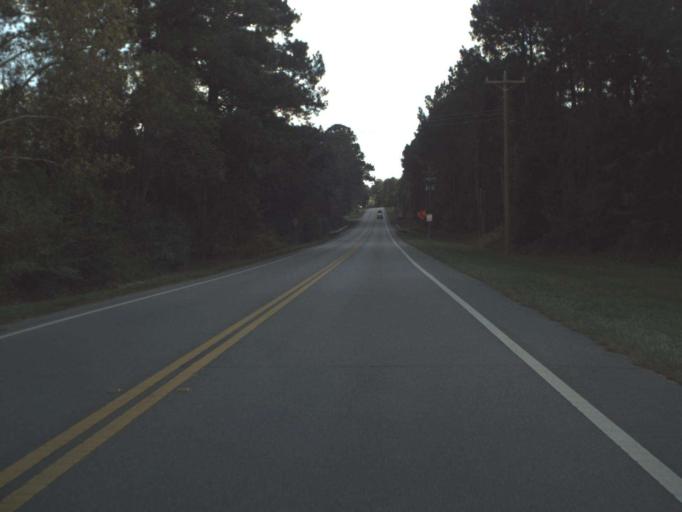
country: US
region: Florida
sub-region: Gadsden County
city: Gretna
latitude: 30.6306
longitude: -84.6711
